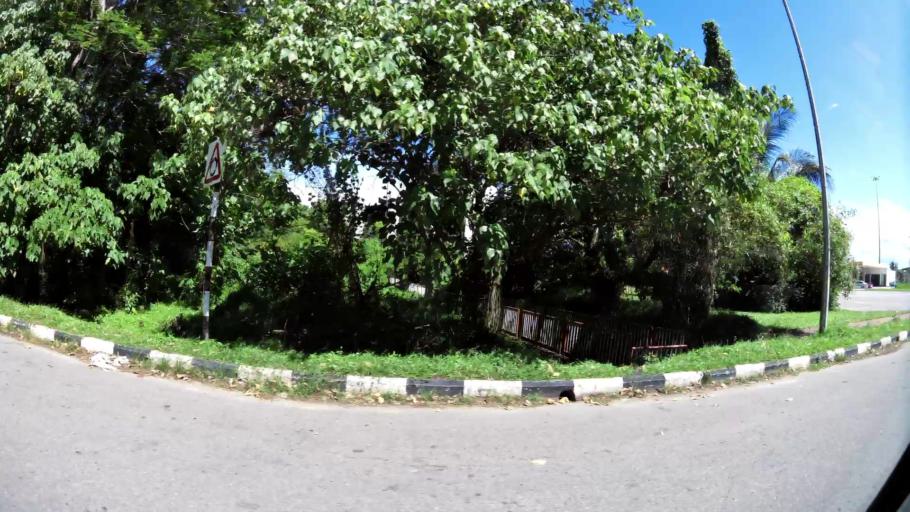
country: BN
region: Brunei and Muara
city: Bandar Seri Begawan
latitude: 5.0272
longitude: 115.0698
